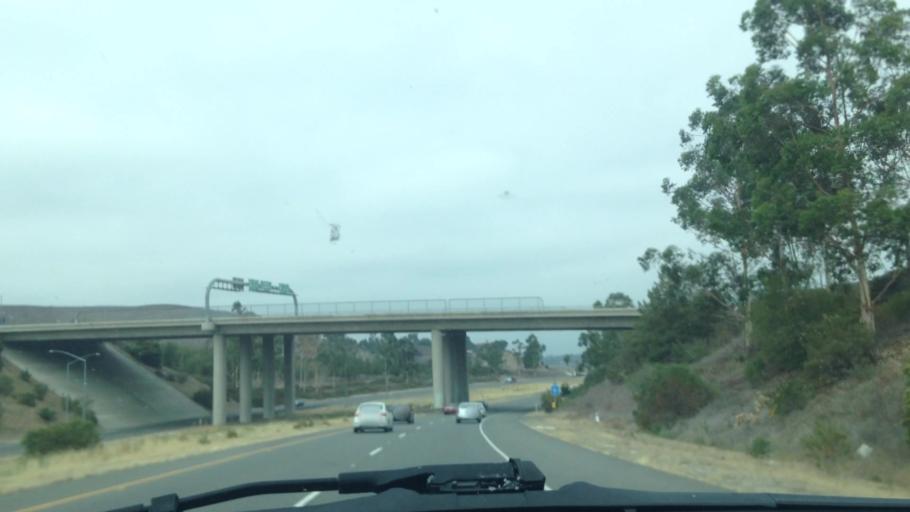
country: US
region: California
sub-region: Orange County
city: North Tustin
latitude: 33.7835
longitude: -117.7483
